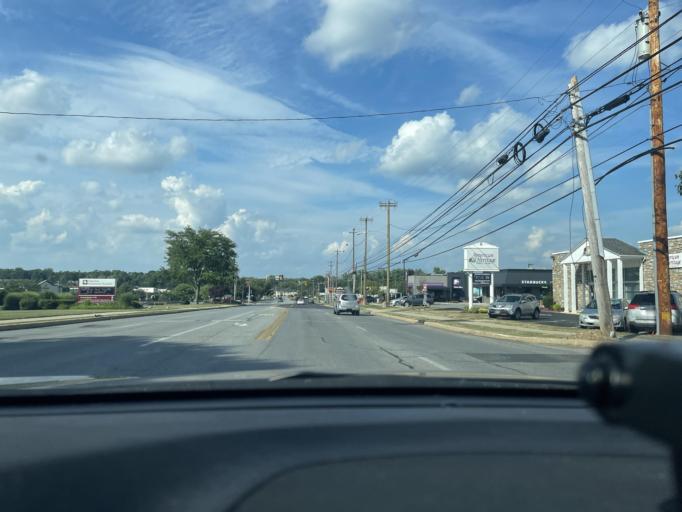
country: US
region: Pennsylvania
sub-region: Montgomery County
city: Norristown
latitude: 40.1391
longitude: -75.3152
